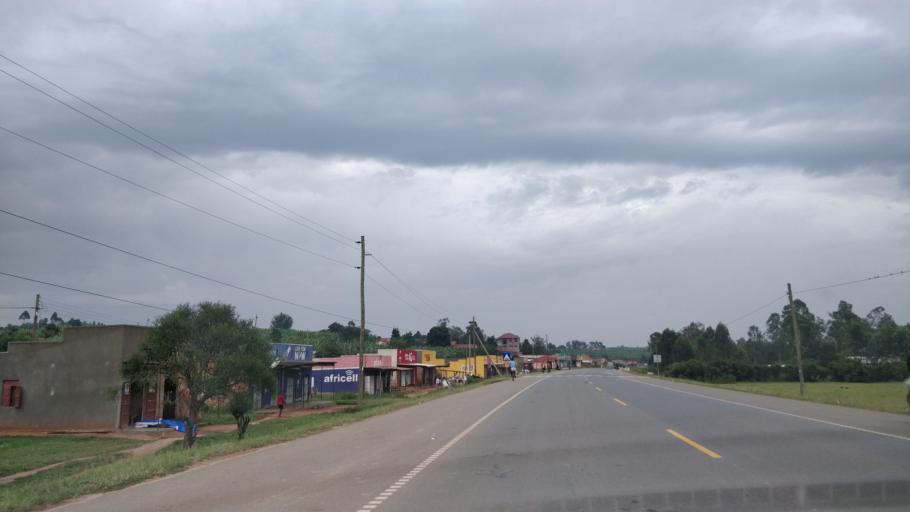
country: UG
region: Western Region
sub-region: Sheema District
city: Kibingo
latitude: -0.6611
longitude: 30.4550
